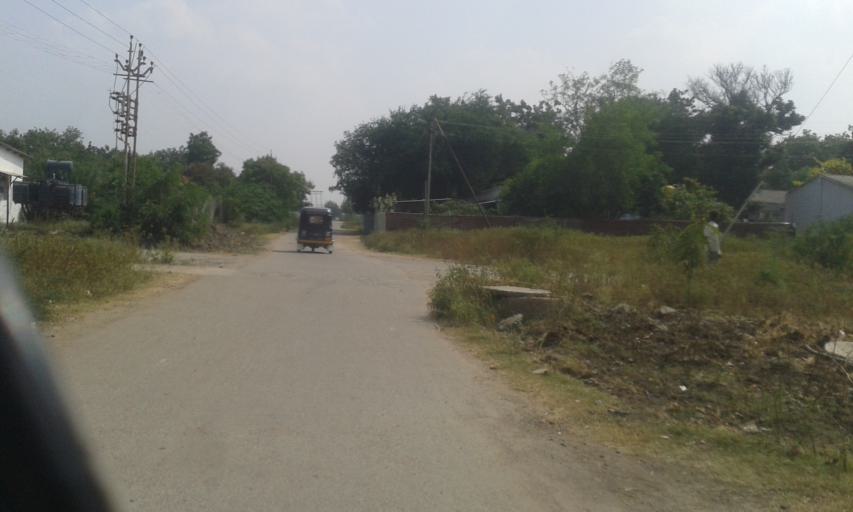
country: IN
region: Karnataka
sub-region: Raichur
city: Lingsugur
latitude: 16.1948
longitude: 76.6597
